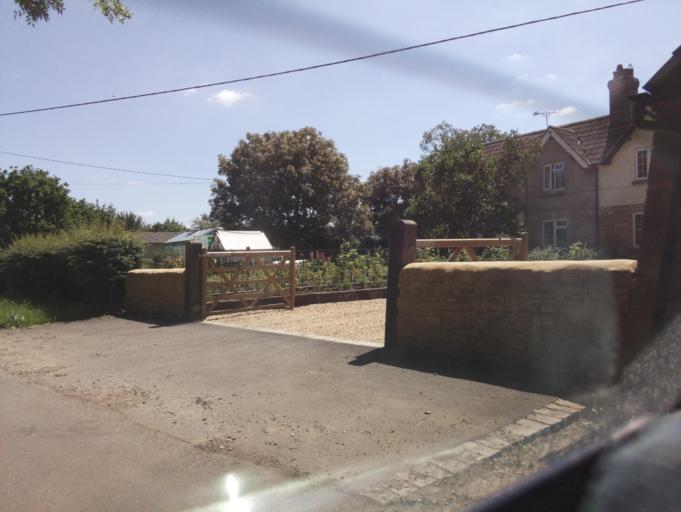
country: GB
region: England
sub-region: Wiltshire
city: Bremhill
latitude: 51.4726
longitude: -2.0529
